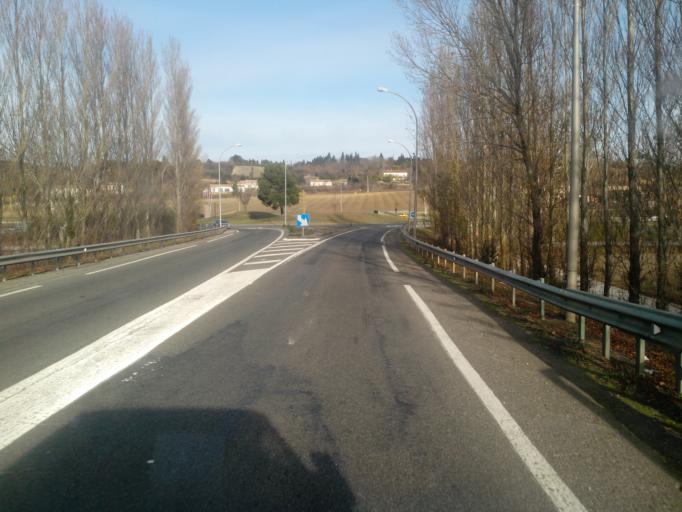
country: FR
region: Languedoc-Roussillon
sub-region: Departement de l'Aude
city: Castelnaudary
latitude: 43.3051
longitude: 1.9786
